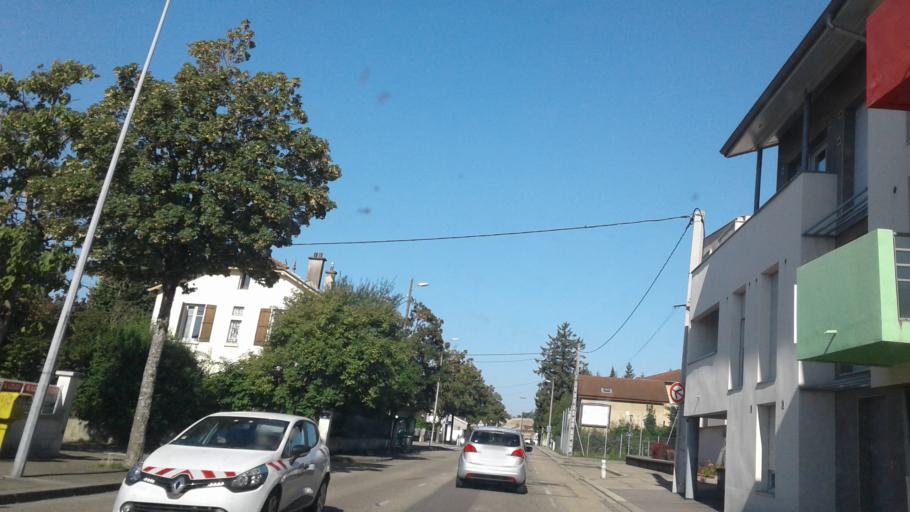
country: FR
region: Rhone-Alpes
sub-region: Departement de l'Ain
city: Bourg-en-Bresse
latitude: 46.1957
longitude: 5.2217
